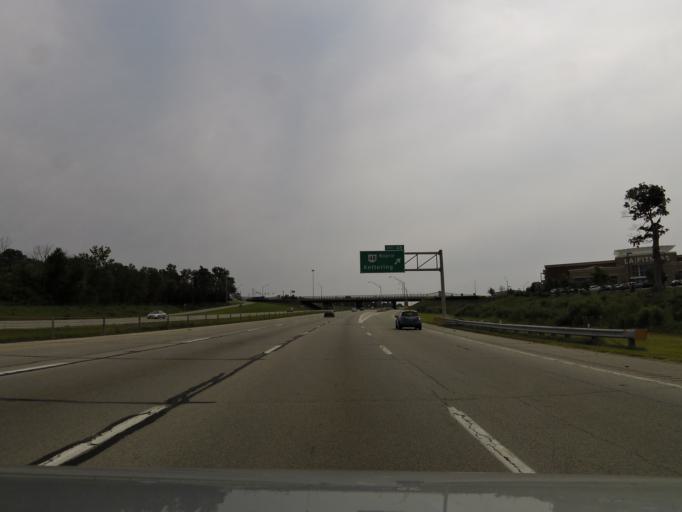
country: US
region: Ohio
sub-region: Montgomery County
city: Centerville
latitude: 39.6449
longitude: -84.1609
